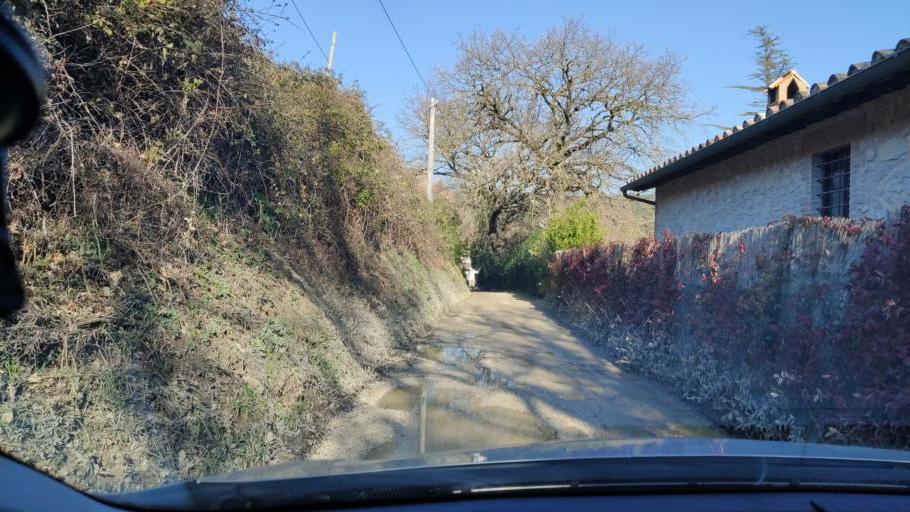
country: IT
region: Umbria
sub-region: Provincia di Terni
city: Fornole
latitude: 42.5558
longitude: 12.4483
